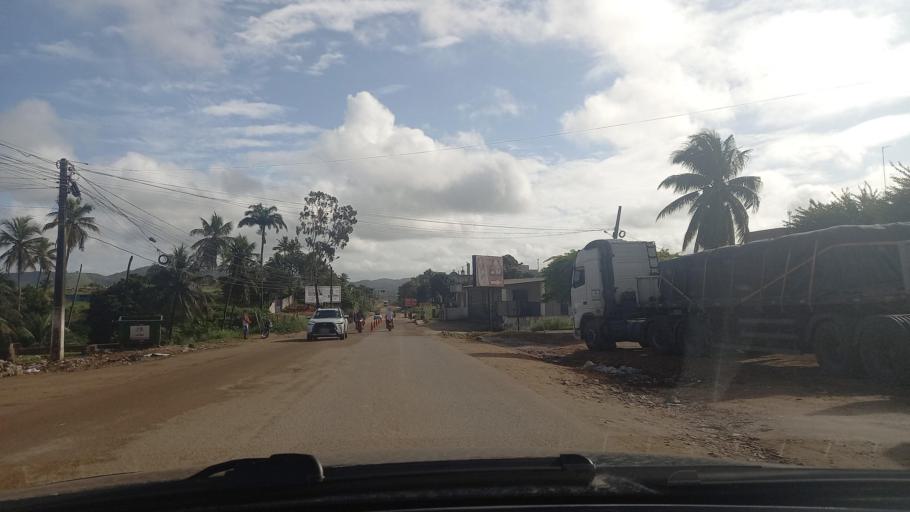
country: BR
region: Pernambuco
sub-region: Vitoria De Santo Antao
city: Vitoria de Santo Antao
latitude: -8.1218
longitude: -35.2822
